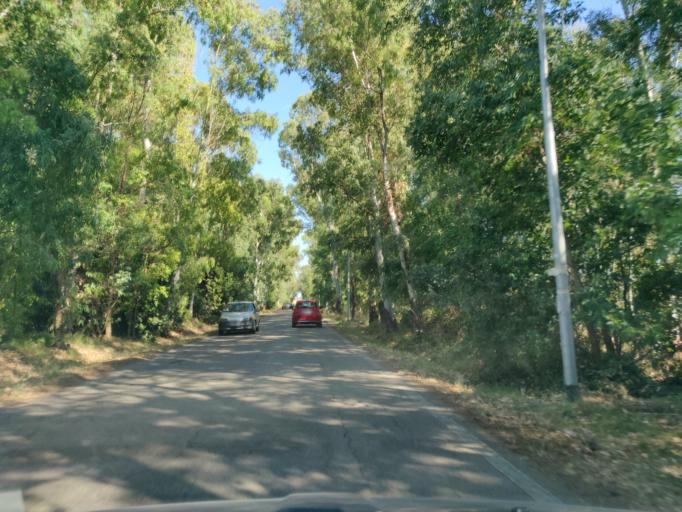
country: IT
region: Latium
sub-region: Citta metropolitana di Roma Capitale
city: Aurelia
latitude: 42.1577
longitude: 11.7518
